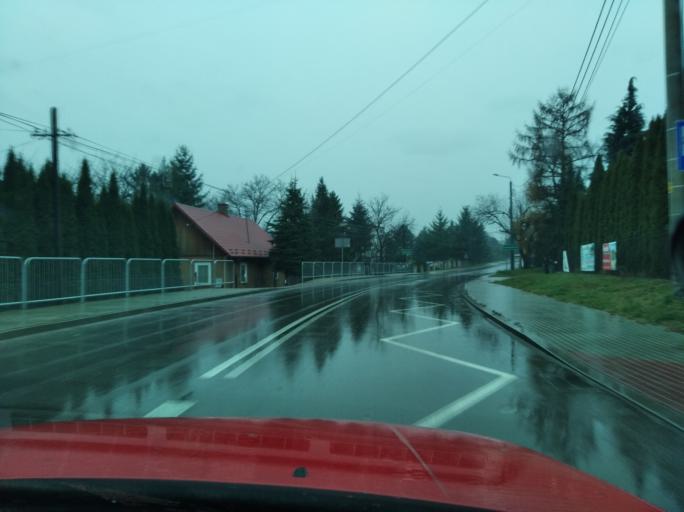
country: PL
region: Subcarpathian Voivodeship
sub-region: Powiat lancucki
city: Lancut
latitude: 50.0706
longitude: 22.2067
